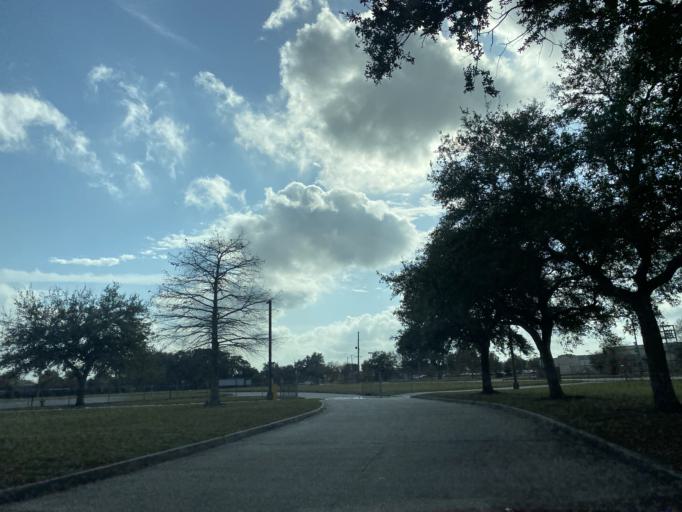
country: US
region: Louisiana
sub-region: Orleans Parish
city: New Orleans
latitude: 30.0298
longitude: -90.0516
